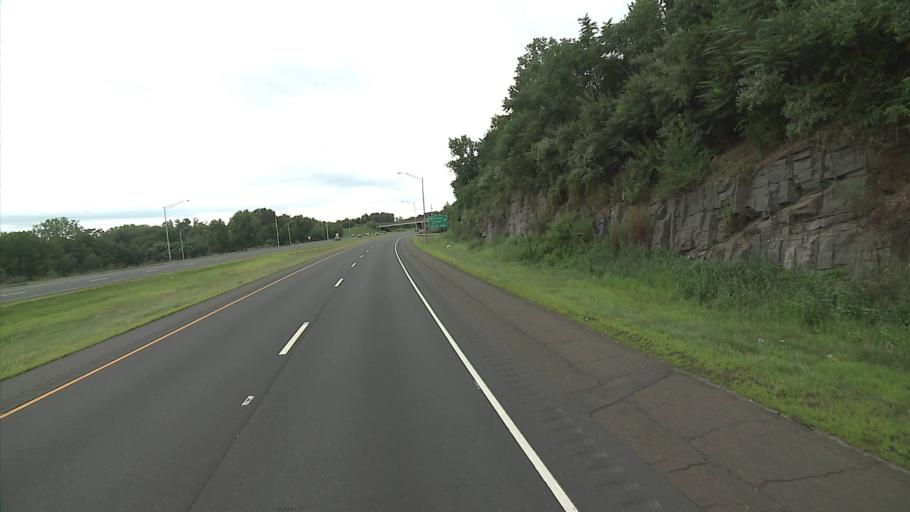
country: US
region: Connecticut
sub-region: Fairfield County
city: Trumbull
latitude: 41.2354
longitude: -73.1545
